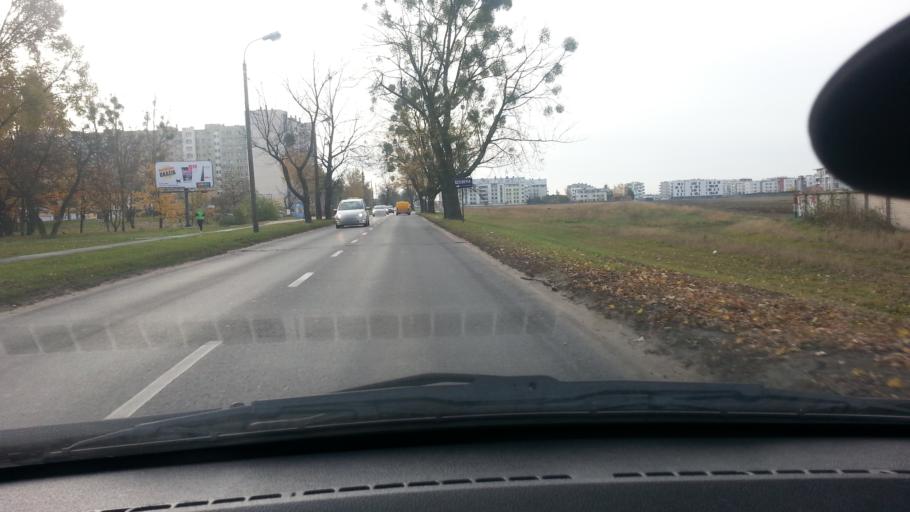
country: PL
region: Masovian Voivodeship
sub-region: Warszawa
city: Bemowo
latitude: 52.2376
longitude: 20.8965
